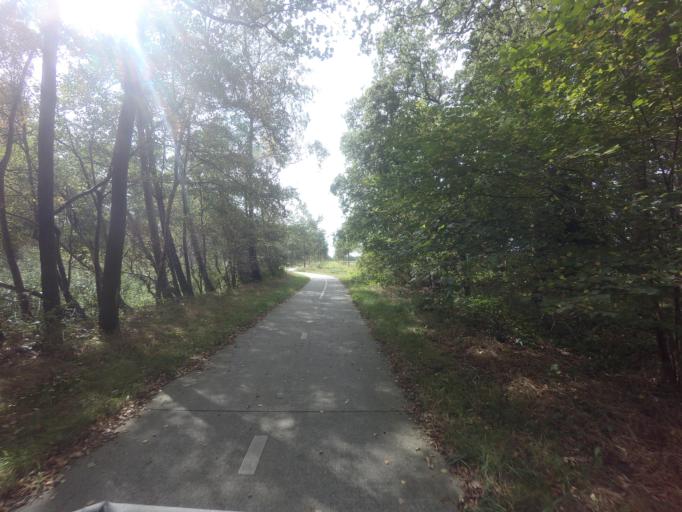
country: NL
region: Groningen
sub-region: Gemeente Leek
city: Leek
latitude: 53.0362
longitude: 6.4245
